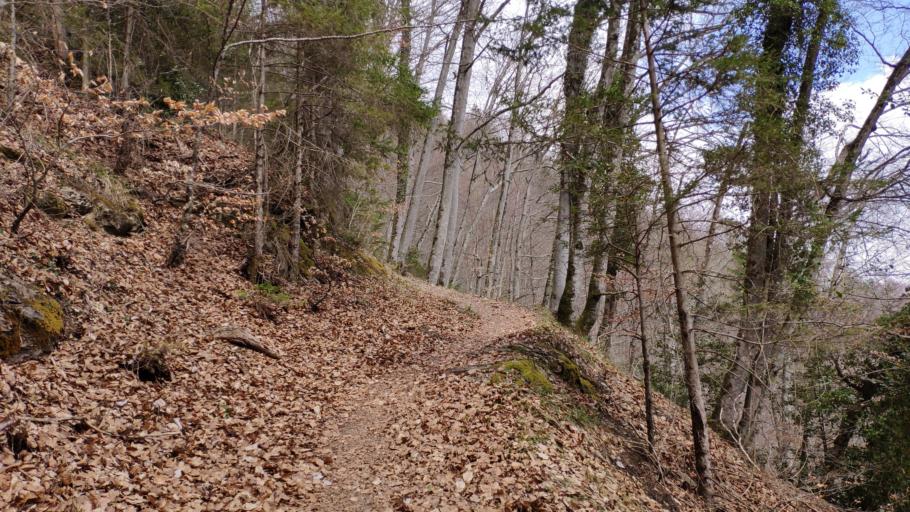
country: CH
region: Bern
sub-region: Interlaken-Oberhasli District
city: Brienz
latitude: 46.7560
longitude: 7.9918
